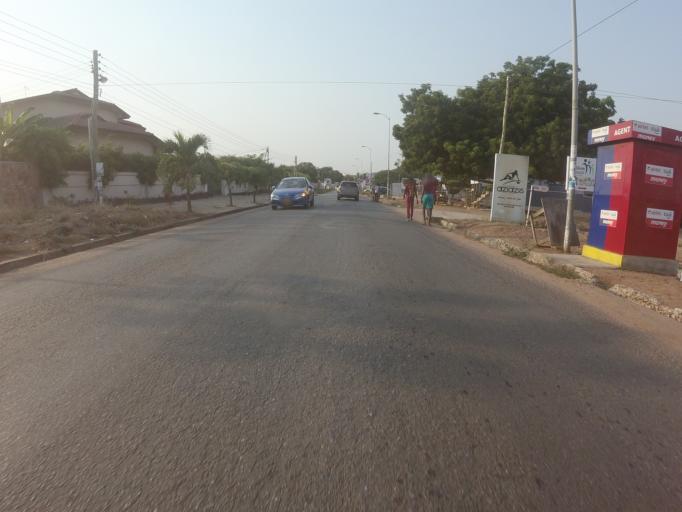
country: GH
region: Greater Accra
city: Nungua
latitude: 5.6210
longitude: -0.0560
